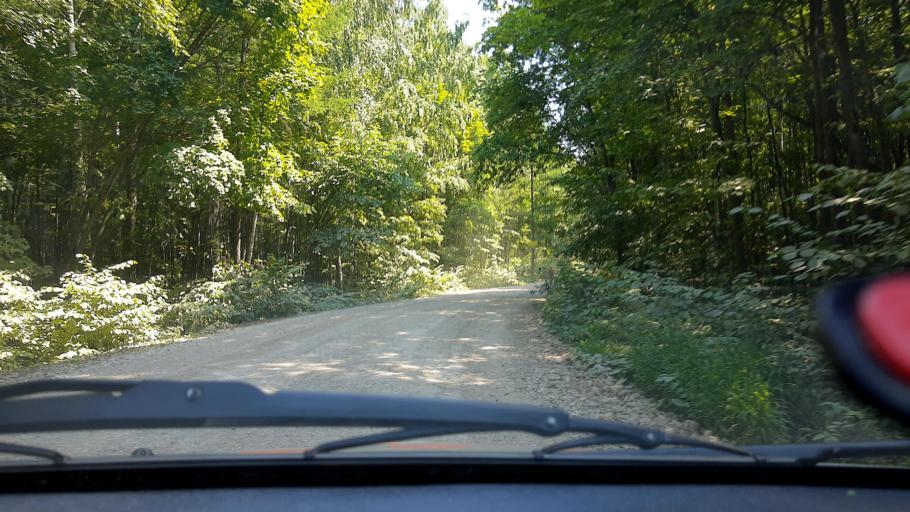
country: RU
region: Bashkortostan
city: Karmaskaly
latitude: 54.3860
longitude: 55.9129
